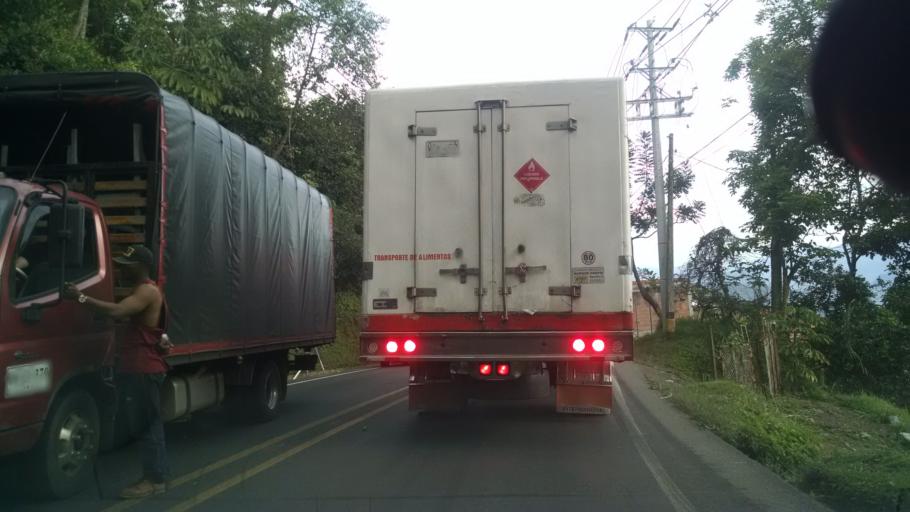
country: CO
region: Antioquia
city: Santa Barbara
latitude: 5.8837
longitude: -75.5718
